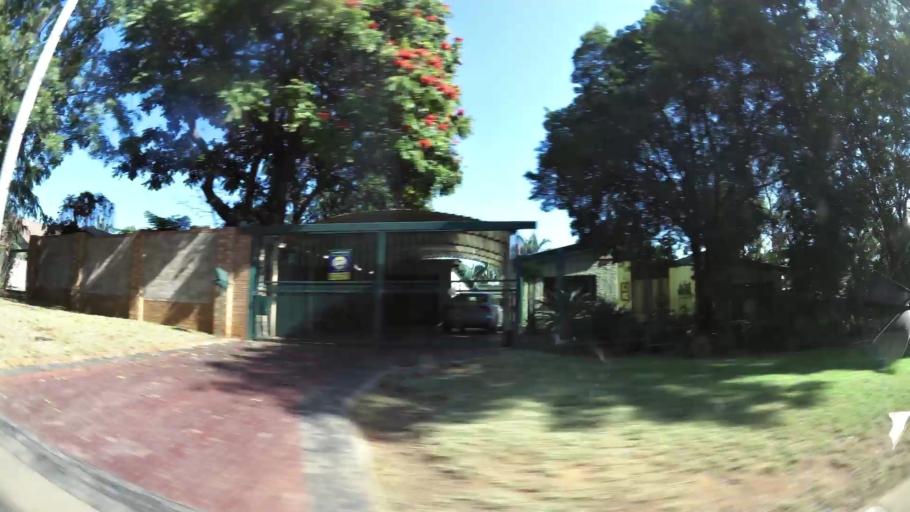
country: ZA
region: Gauteng
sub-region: City of Tshwane Metropolitan Municipality
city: Pretoria
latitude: -25.6857
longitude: 28.2253
